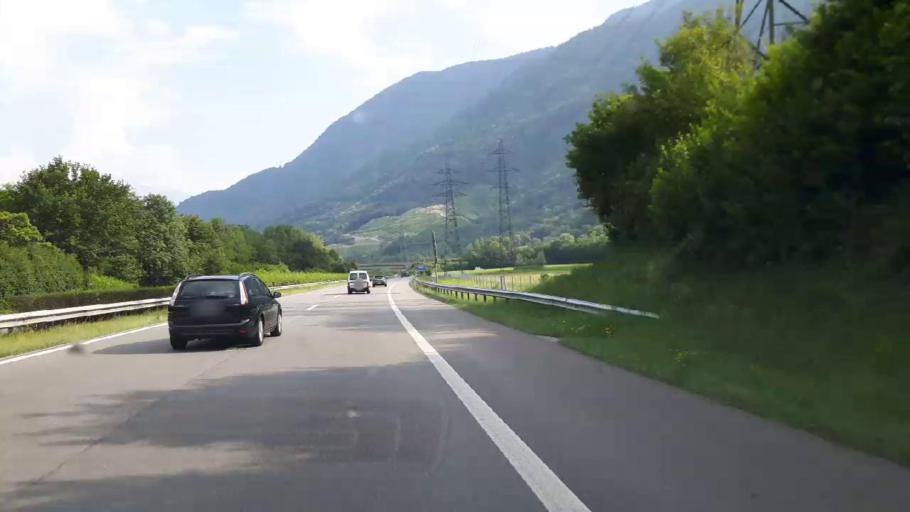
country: CH
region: Ticino
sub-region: Riviera District
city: Claro
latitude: 46.2601
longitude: 9.0096
